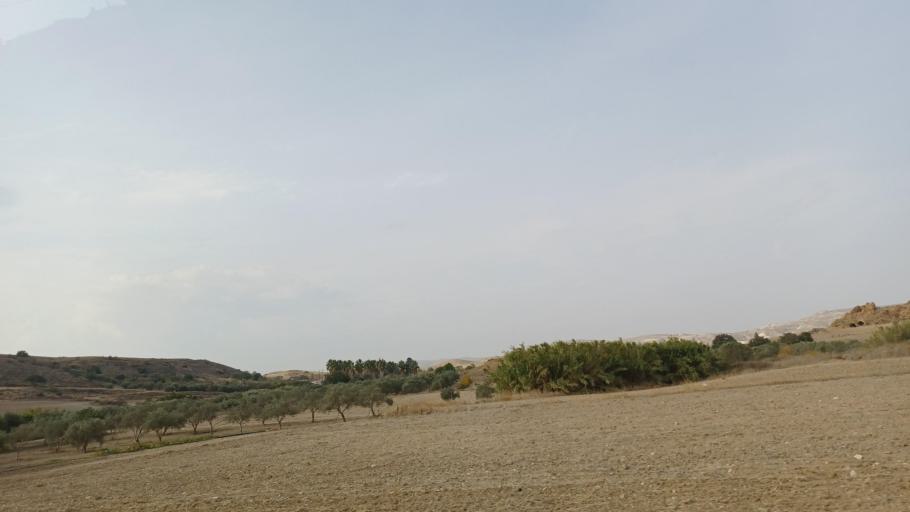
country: CY
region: Larnaka
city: Troulloi
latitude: 35.0267
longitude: 33.6124
